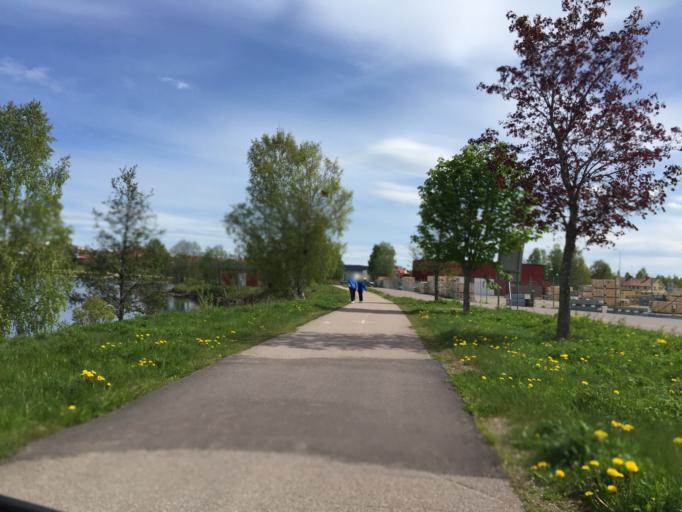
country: SE
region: Dalarna
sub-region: Ludvika Kommun
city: Ludvika
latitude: 60.1481
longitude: 15.1732
